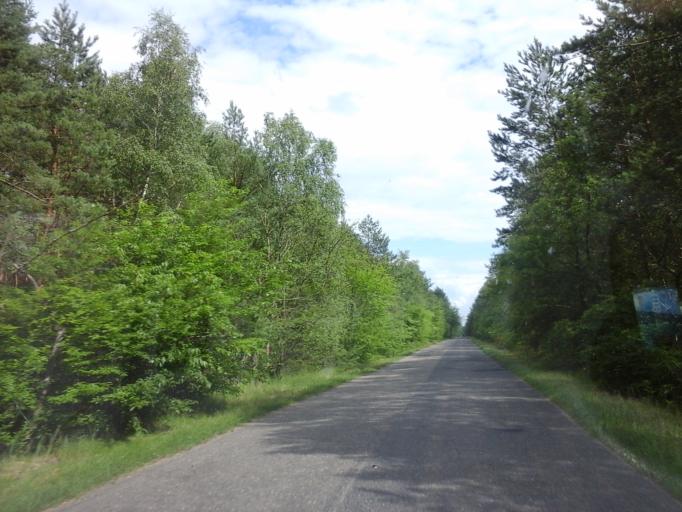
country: PL
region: West Pomeranian Voivodeship
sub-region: Powiat goleniowski
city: Goleniow
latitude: 53.4569
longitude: 14.8571
